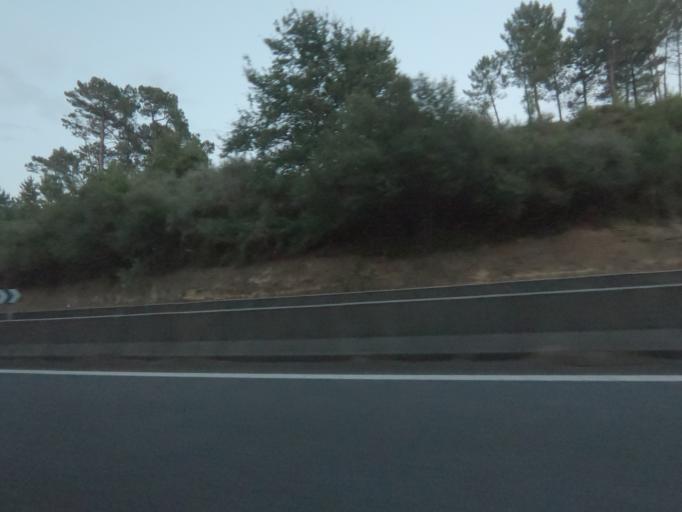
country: ES
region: Galicia
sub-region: Provincia de Pontevedra
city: Tui
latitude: 42.0786
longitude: -8.6327
